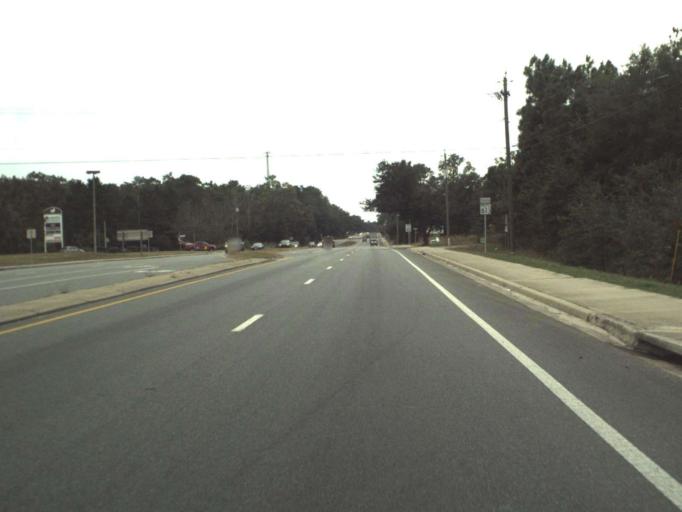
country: US
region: Florida
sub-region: Leon County
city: Tallahassee
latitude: 30.3750
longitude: -84.2932
